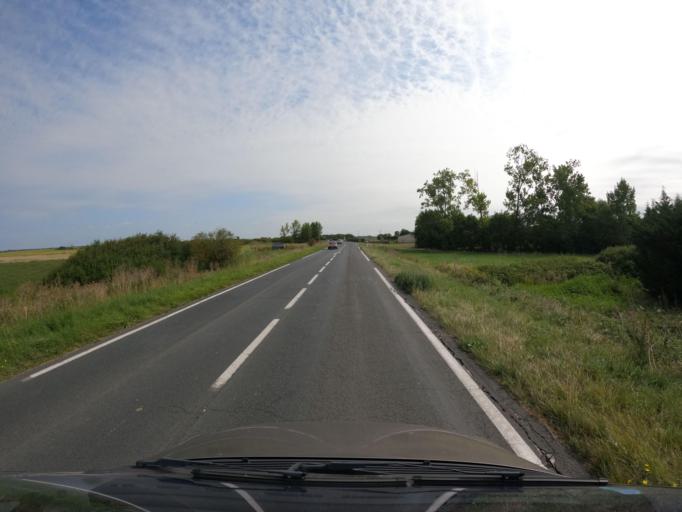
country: FR
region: Pays de la Loire
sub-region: Departement de la Vendee
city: Triaize
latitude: 46.3725
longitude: -1.2061
